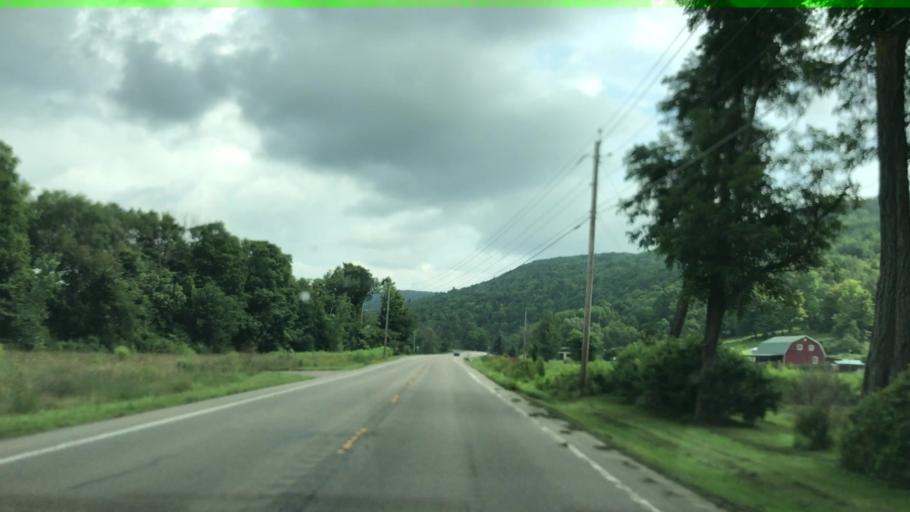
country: US
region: New York
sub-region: Steuben County
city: Bath
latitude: 42.3881
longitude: -77.3537
